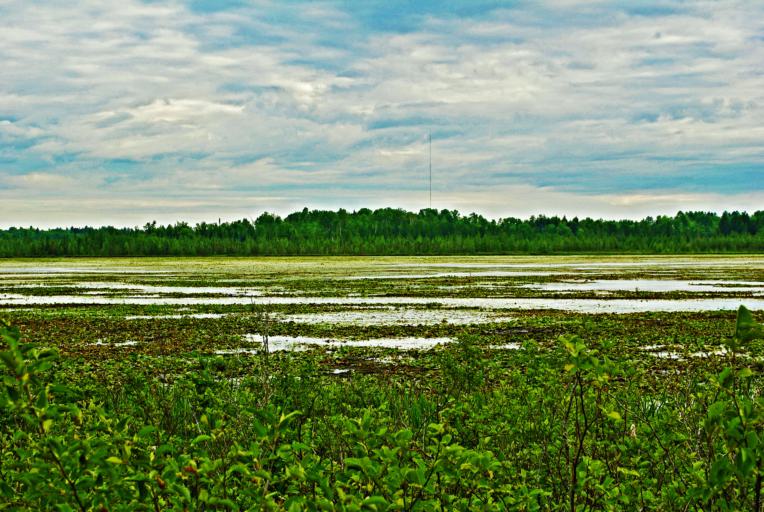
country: US
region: Wisconsin
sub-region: Vilas County
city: Eagle River
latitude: 45.7237
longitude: -89.1548
